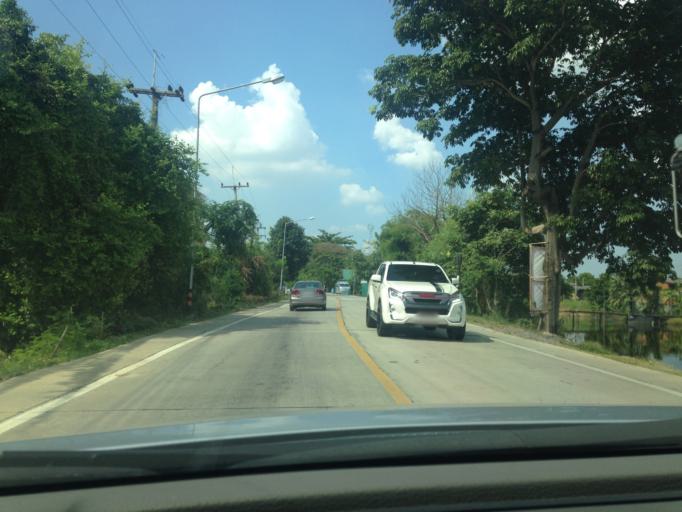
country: TH
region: Pathum Thani
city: Khlong Luang
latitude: 14.0551
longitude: 100.5900
